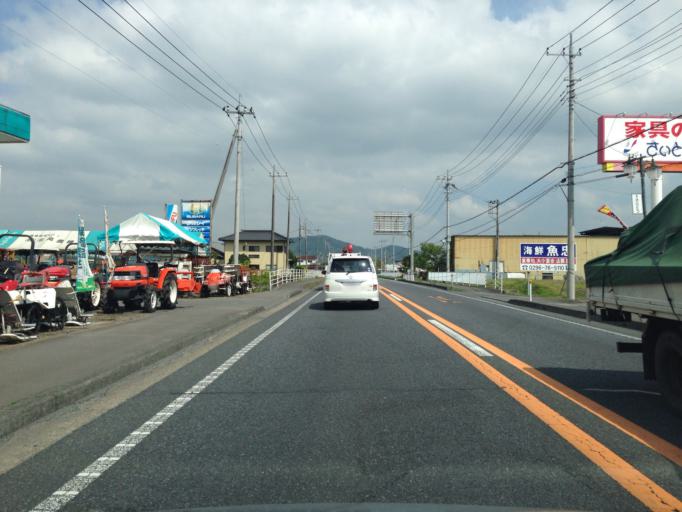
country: JP
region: Ibaraki
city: Iwase
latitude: 36.3590
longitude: 140.1268
